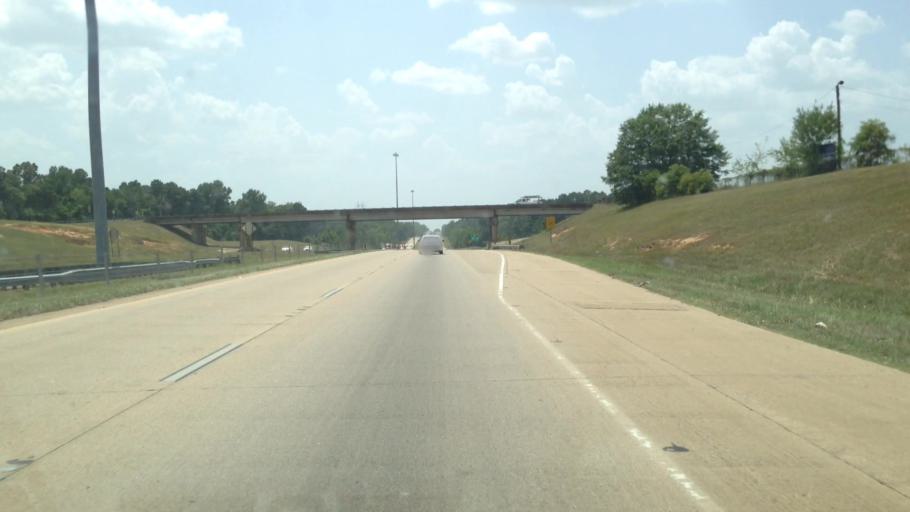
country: US
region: Louisiana
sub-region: Lincoln Parish
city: Grambling
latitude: 32.5415
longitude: -92.7104
